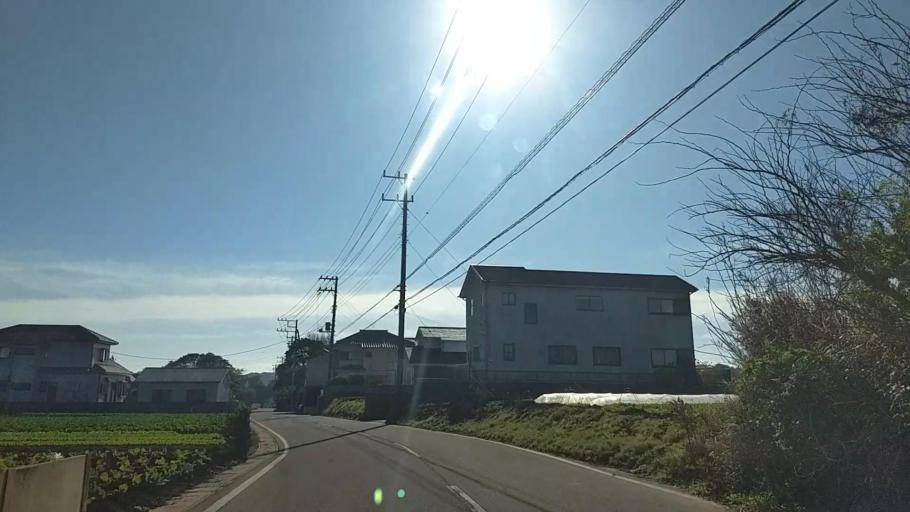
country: JP
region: Chiba
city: Hasaki
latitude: 35.7185
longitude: 140.8458
